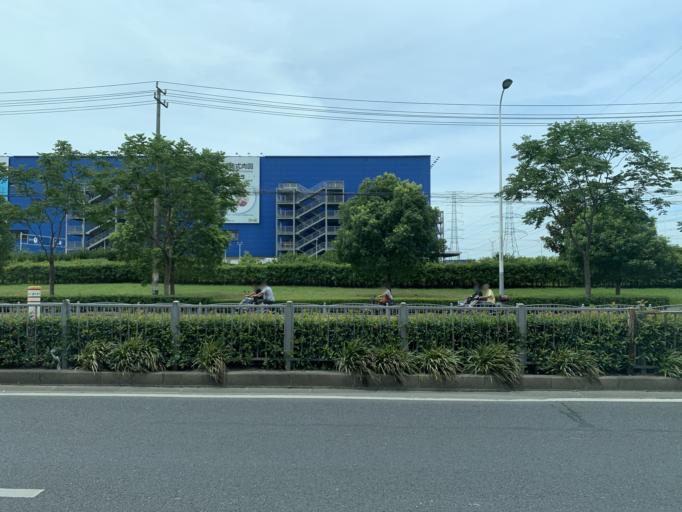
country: CN
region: Shanghai Shi
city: Kangqiao
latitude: 31.1626
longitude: 121.5595
